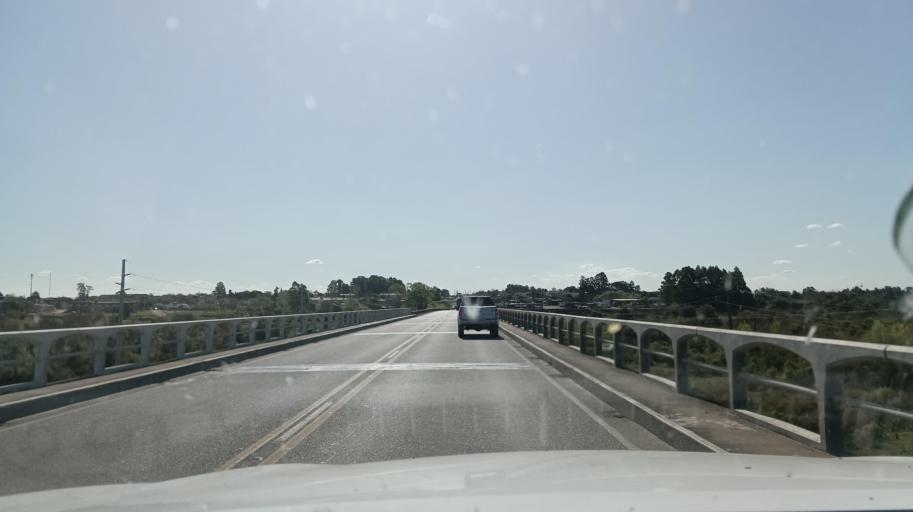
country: UY
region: Florida
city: Florida
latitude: -34.0905
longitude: -56.2045
